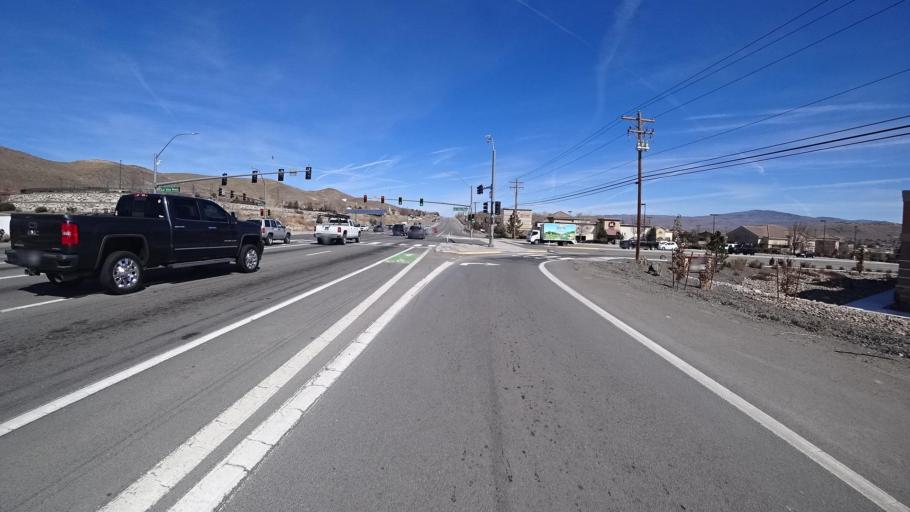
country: US
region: Nevada
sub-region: Washoe County
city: Sun Valley
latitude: 39.5830
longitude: -119.7433
